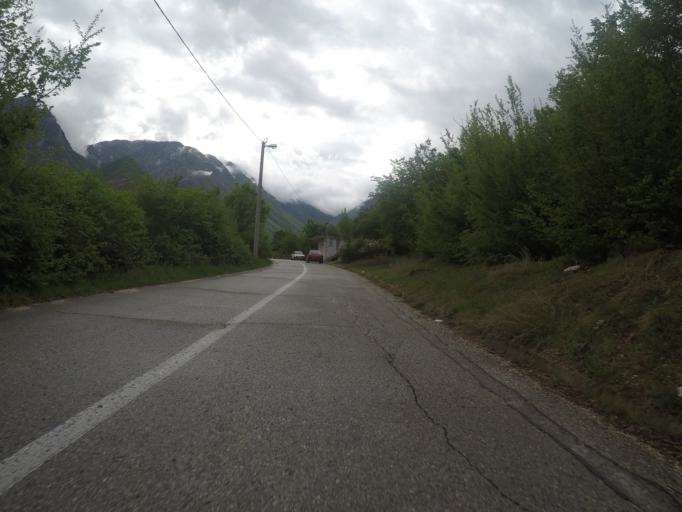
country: BA
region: Federation of Bosnia and Herzegovina
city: Siroki Brijeg
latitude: 43.5406
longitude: 17.5875
